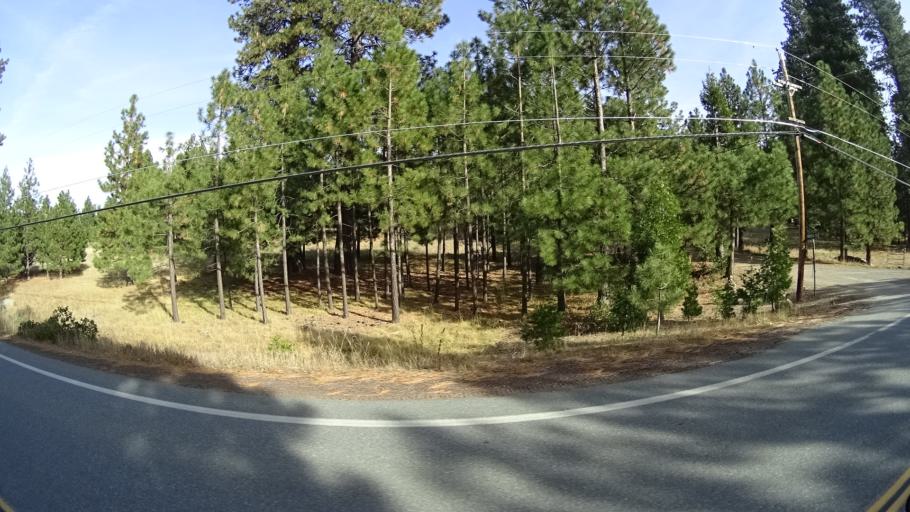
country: US
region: California
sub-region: Siskiyou County
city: Weed
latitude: 41.3860
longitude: -122.4091
